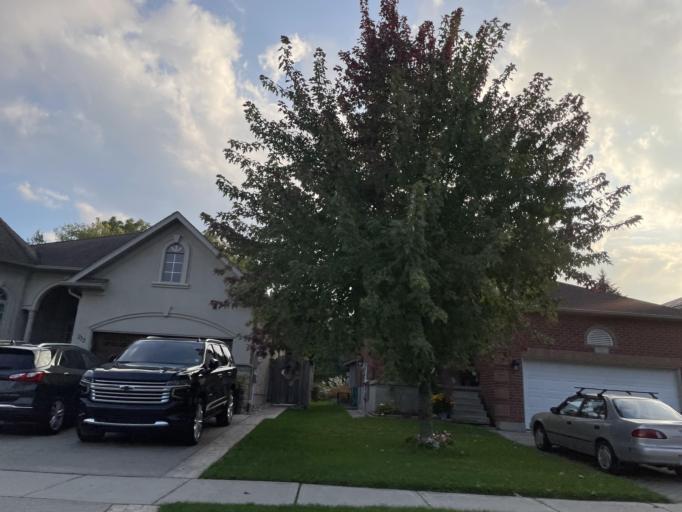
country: CA
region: Ontario
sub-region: Wellington County
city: Guelph
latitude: 43.5249
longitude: -80.2725
